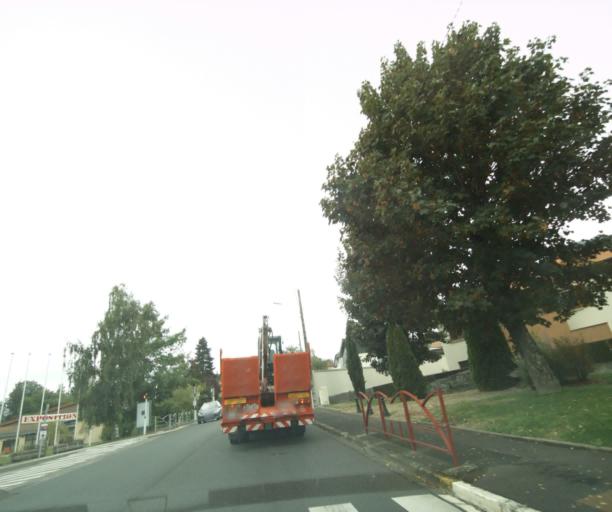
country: FR
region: Auvergne
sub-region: Departement du Puy-de-Dome
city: Ceyrat
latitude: 45.7398
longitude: 3.0596
